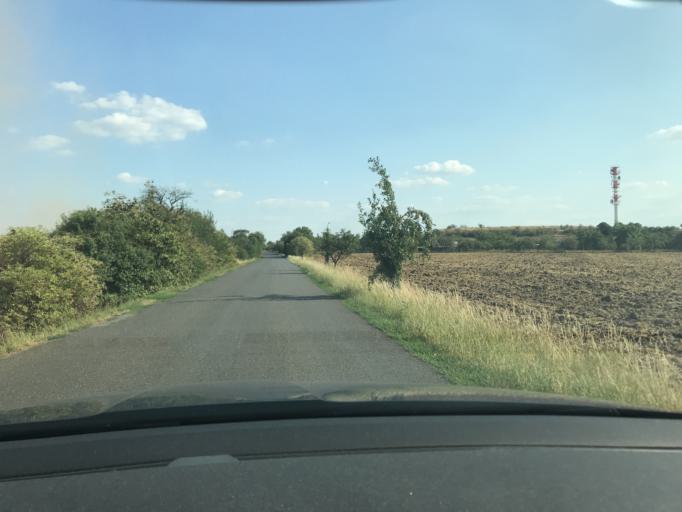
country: CZ
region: Central Bohemia
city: Kralupy nad Vltavou
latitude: 50.2313
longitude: 14.3160
